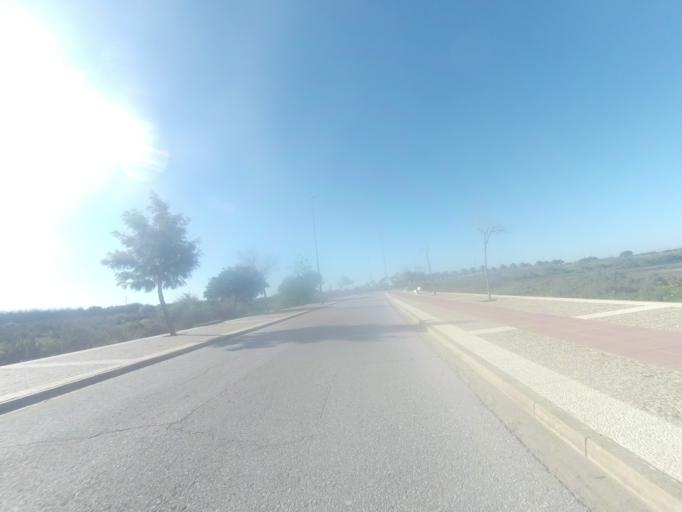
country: ES
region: Andalusia
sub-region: Provincia de Huelva
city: Palos de la Frontera
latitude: 37.2303
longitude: -6.9044
